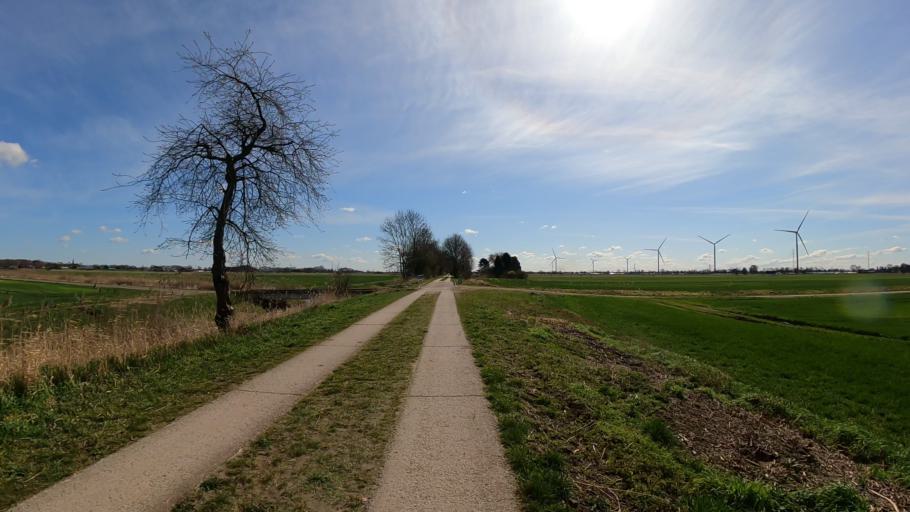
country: DE
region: Hamburg
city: Rothenburgsort
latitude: 53.4703
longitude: 10.0893
